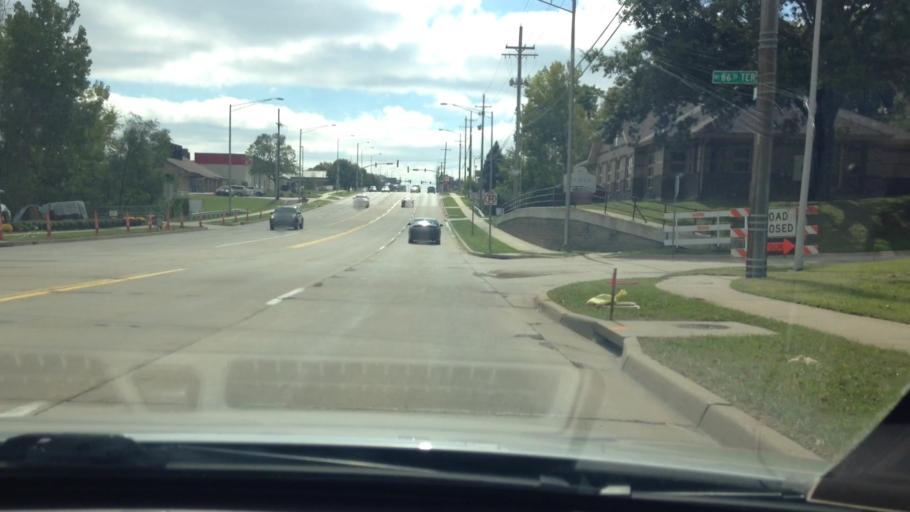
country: US
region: Missouri
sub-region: Clay County
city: Gladstone
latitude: 39.2508
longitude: -94.5759
